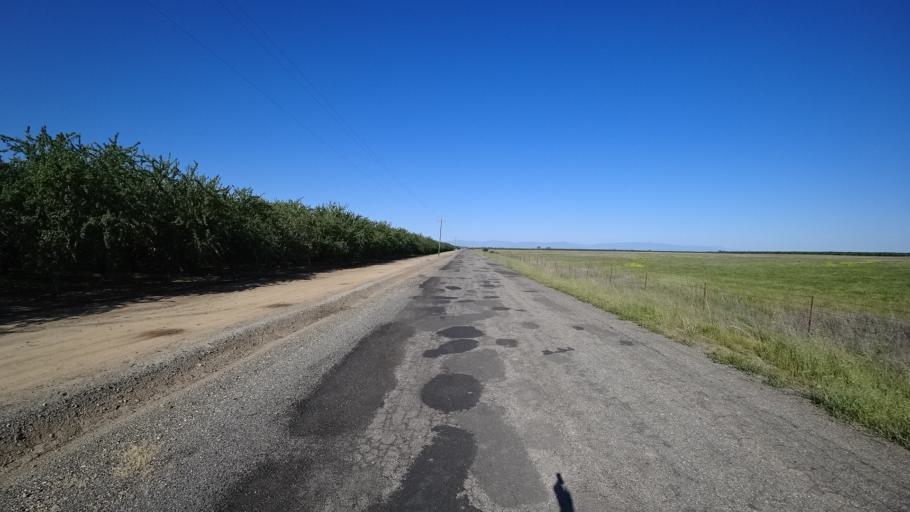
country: US
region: California
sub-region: Glenn County
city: Hamilton City
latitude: 39.6781
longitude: -122.0324
